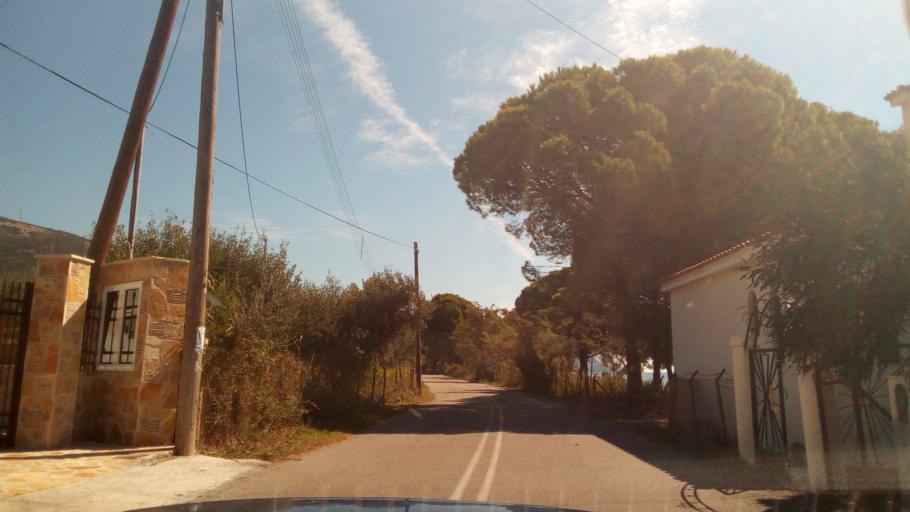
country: GR
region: West Greece
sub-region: Nomos Achaias
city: Selianitika
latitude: 38.3754
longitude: 22.0837
